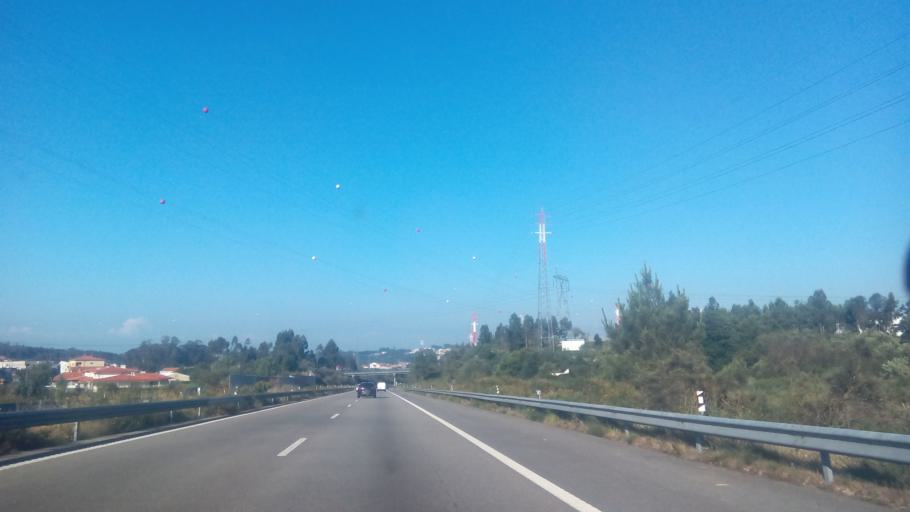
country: PT
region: Porto
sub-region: Pacos de Ferreira
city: Seroa
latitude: 41.2542
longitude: -8.4235
